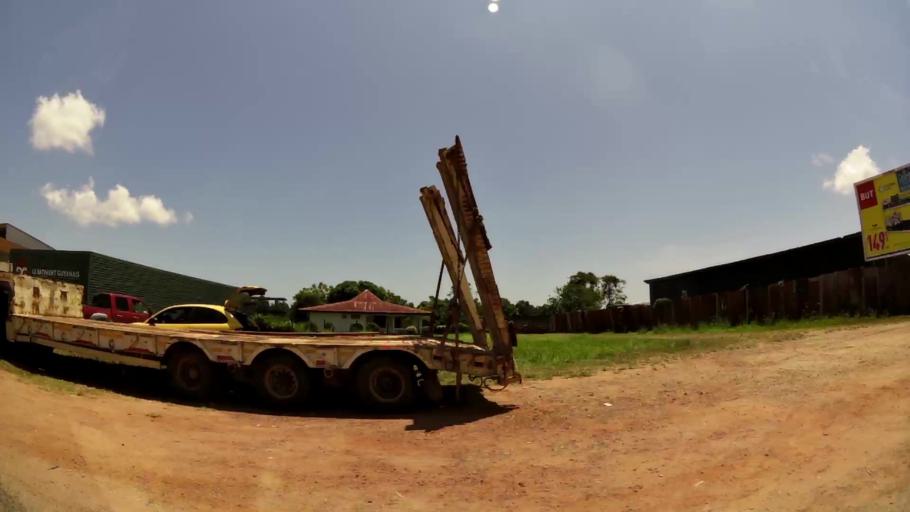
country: GF
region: Guyane
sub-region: Guyane
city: Cayenne
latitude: 4.8972
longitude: -52.3341
